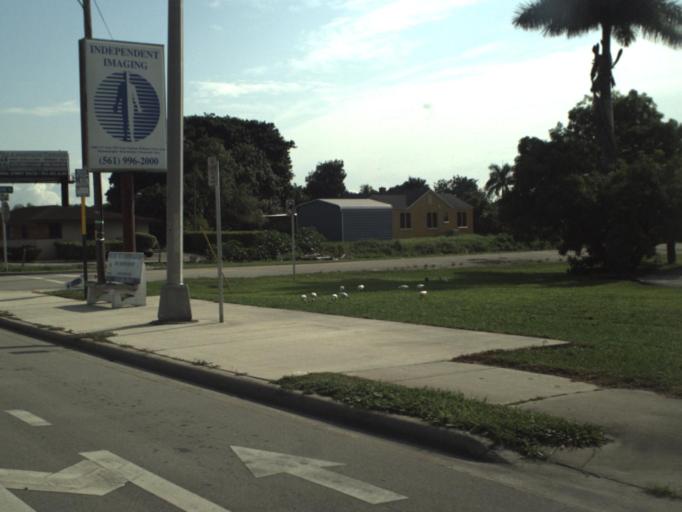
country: US
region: Florida
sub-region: Palm Beach County
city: Belle Glade
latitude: 26.6780
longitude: -80.6702
